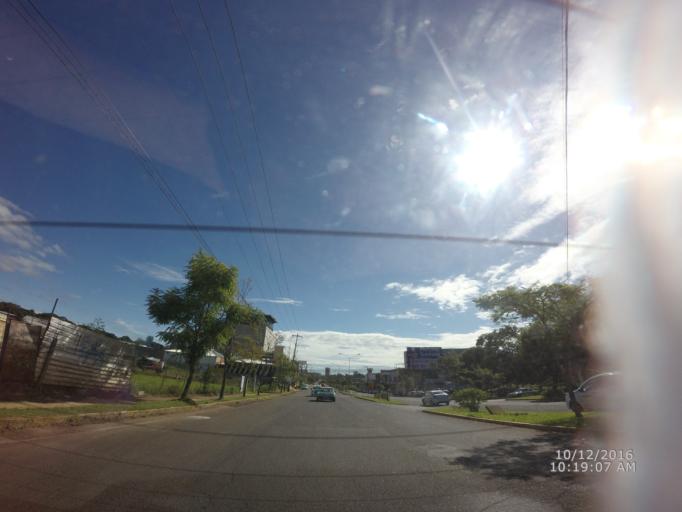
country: TR
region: Sivas
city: Karayun
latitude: 39.6707
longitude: 37.2662
